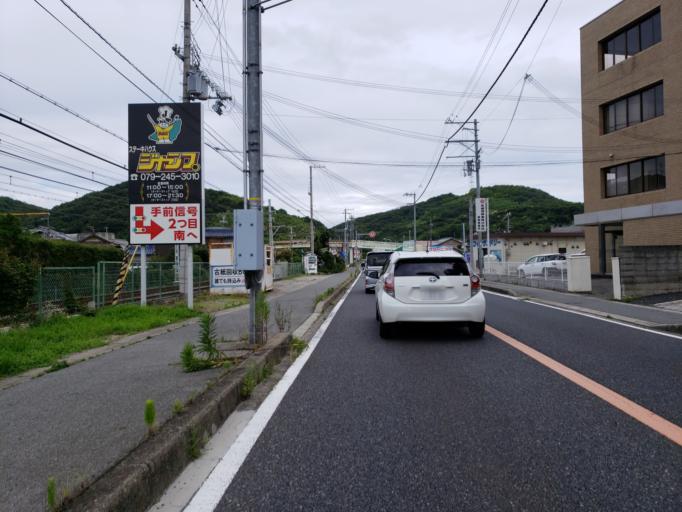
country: JP
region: Hyogo
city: Shirahamacho-usazakiminami
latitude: 34.7834
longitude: 134.7237
